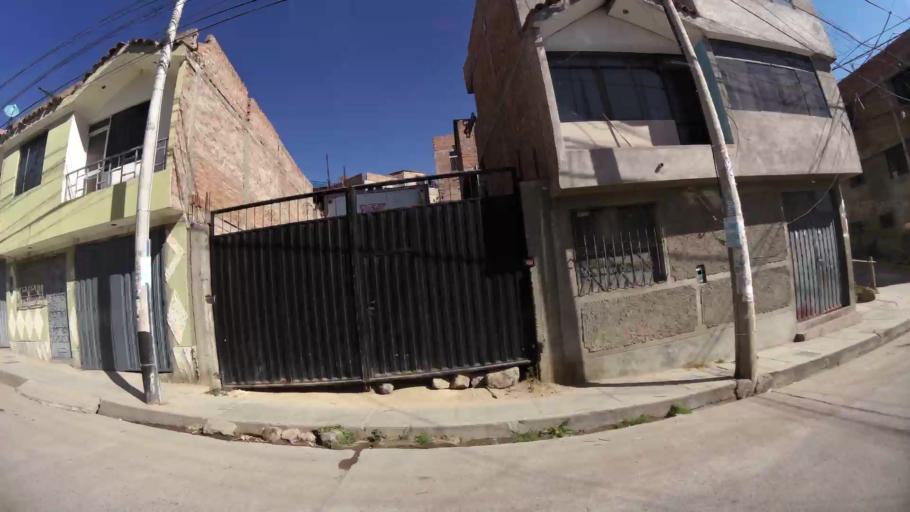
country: PE
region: Ayacucho
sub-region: Provincia de Huamanga
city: Ayacucho
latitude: -13.1651
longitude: -74.2331
